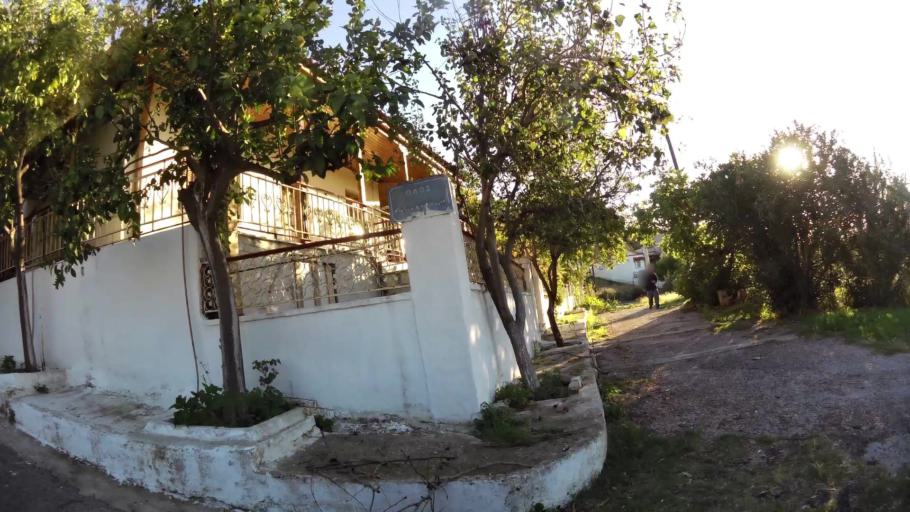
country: GR
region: Attica
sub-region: Nomarchia Athinas
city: Skaramangas
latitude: 38.0275
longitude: 23.6168
